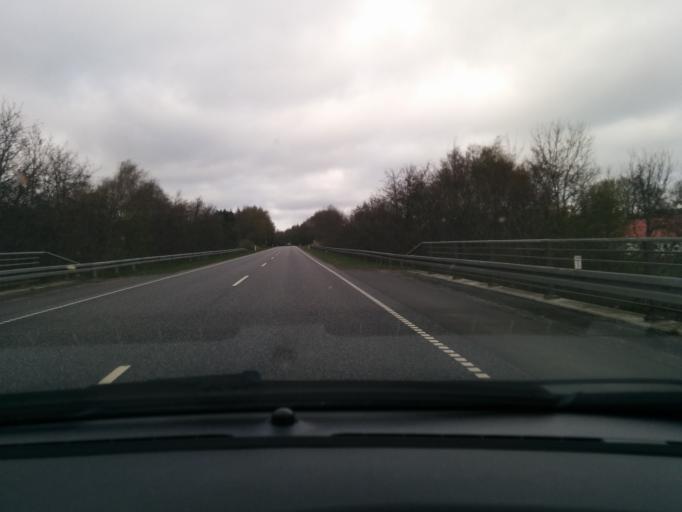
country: DK
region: Central Jutland
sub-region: Favrskov Kommune
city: Hammel
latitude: 56.2510
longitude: 9.8781
